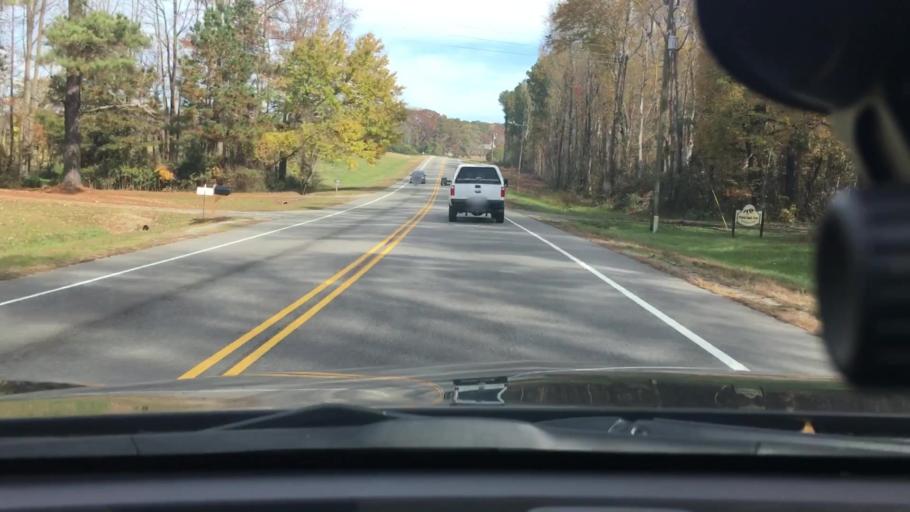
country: US
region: North Carolina
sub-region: Lee County
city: Sanford
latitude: 35.3840
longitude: -79.2756
